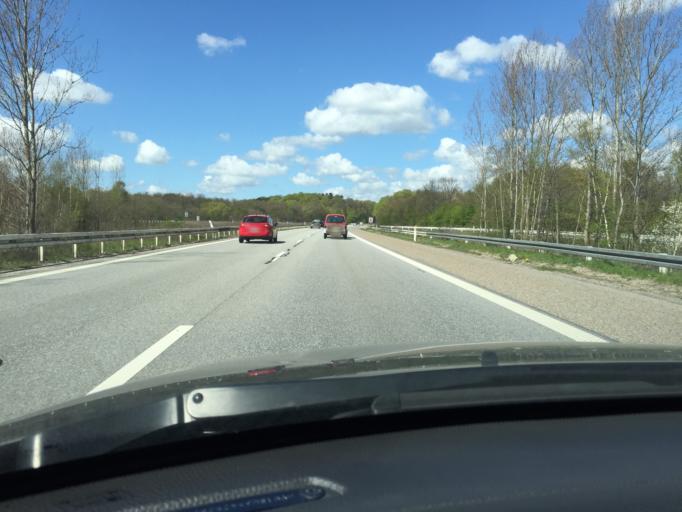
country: DK
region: Capital Region
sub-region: Fureso Kommune
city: Vaerlose
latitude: 55.7798
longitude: 12.3986
